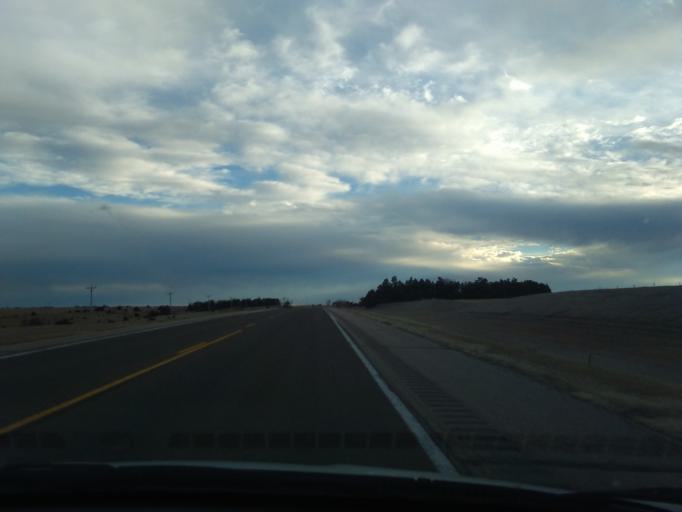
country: US
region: Nebraska
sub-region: Phelps County
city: Holdrege
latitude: 40.3162
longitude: -99.3684
